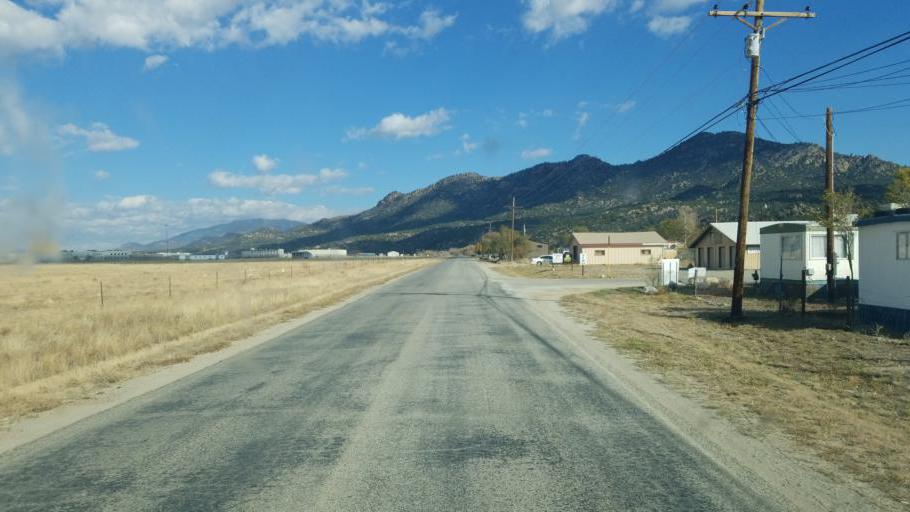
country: US
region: Colorado
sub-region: Chaffee County
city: Buena Vista
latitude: 38.8151
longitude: -106.1100
